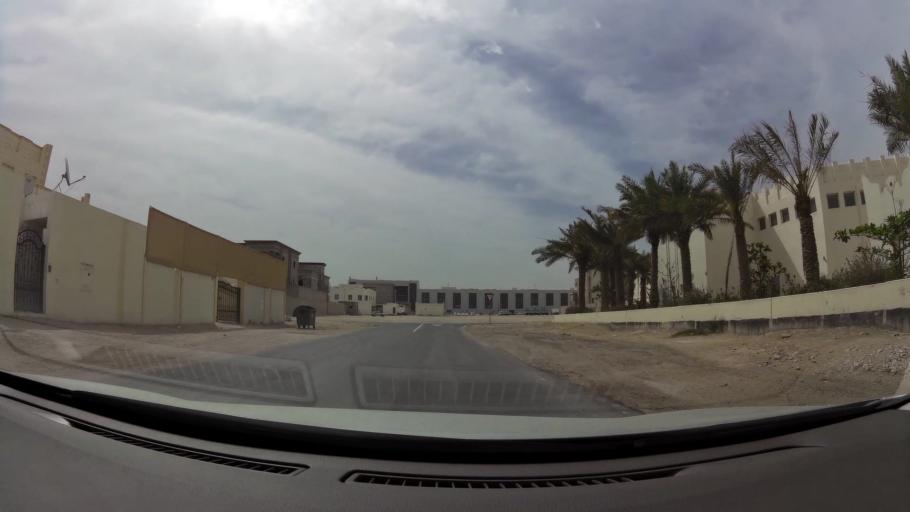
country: QA
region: Al Wakrah
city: Al Wukayr
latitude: 25.2027
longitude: 51.4692
